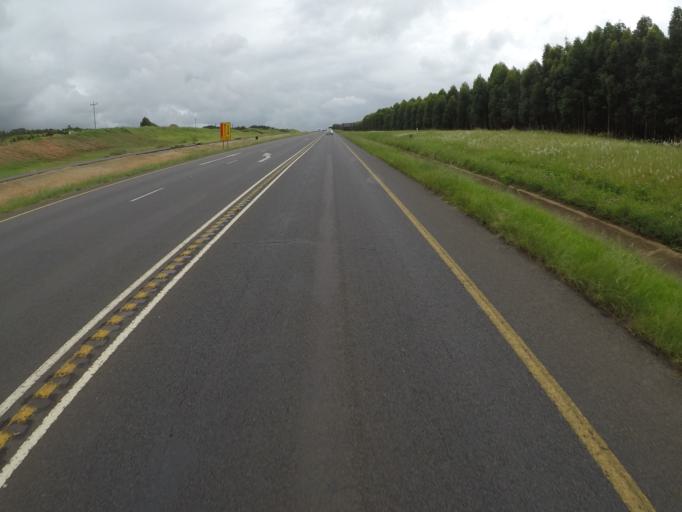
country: ZA
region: KwaZulu-Natal
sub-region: uThungulu District Municipality
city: Empangeni
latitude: -28.8038
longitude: 31.9185
